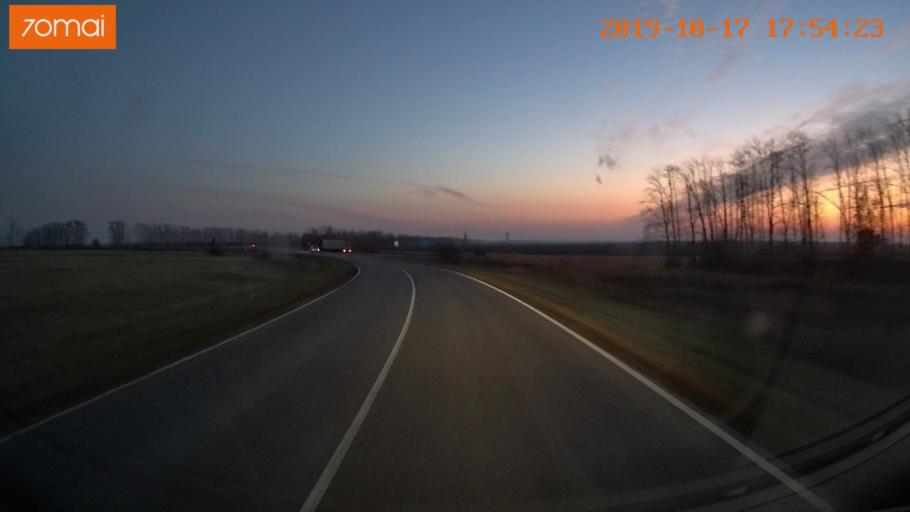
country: RU
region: Tula
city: Kurkino
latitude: 53.6084
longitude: 38.6665
